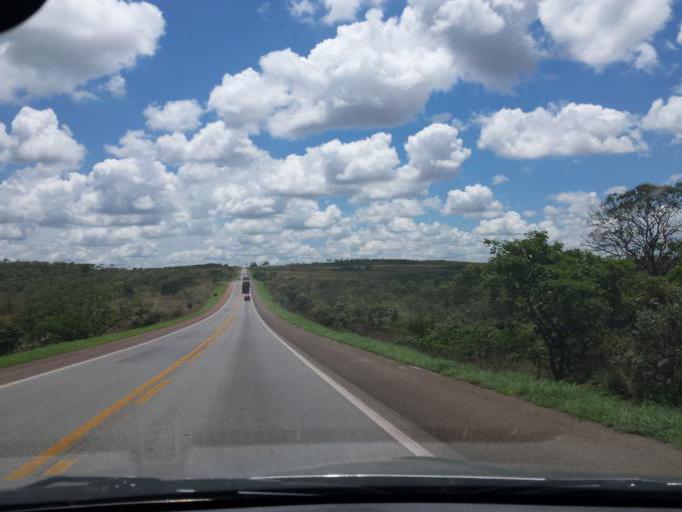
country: BR
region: Goias
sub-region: Cristalina
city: Cristalina
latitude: -16.7234
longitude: -47.6447
